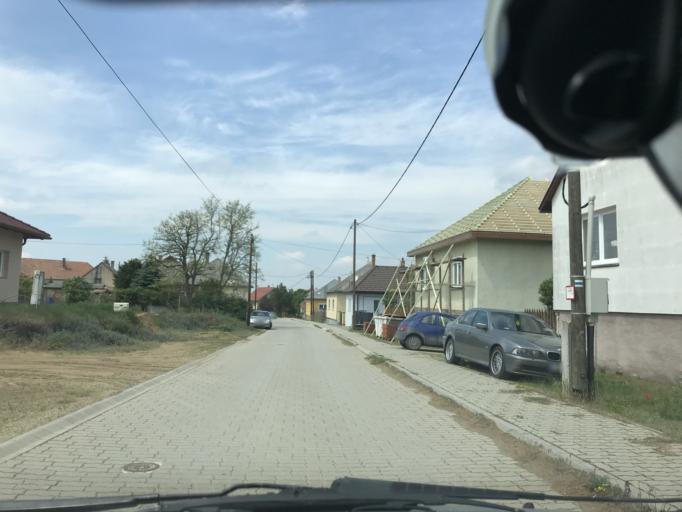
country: HU
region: Komarom-Esztergom
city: Piliscsev
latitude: 47.6704
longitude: 18.8193
